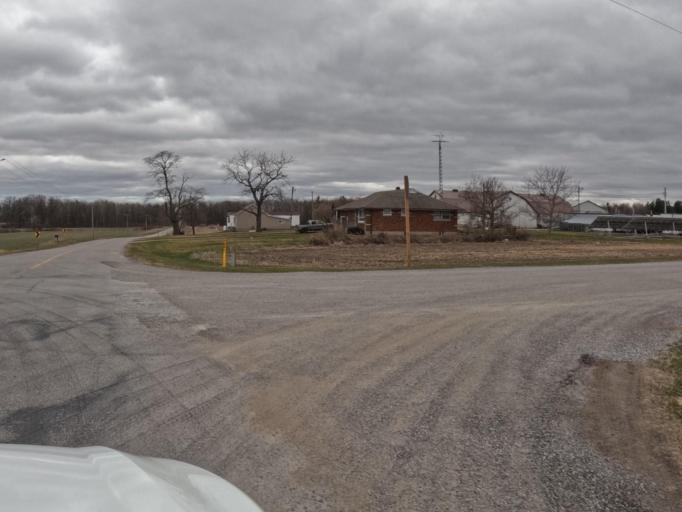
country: CA
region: Ontario
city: Norfolk County
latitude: 42.9571
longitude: -80.3952
